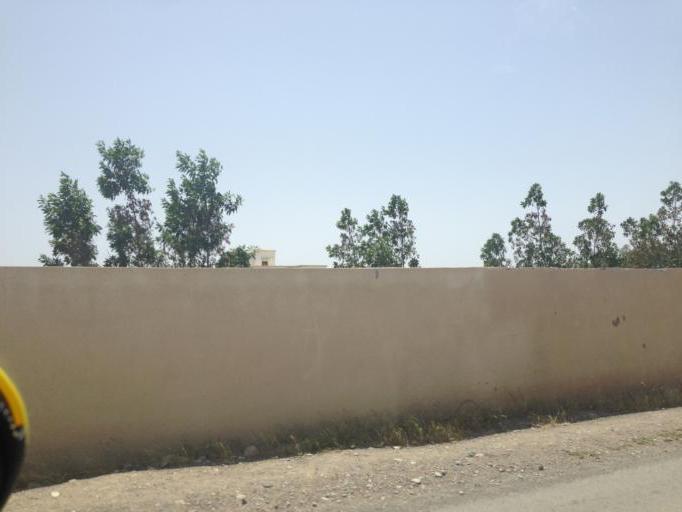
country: OM
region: Muhafazat Masqat
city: As Sib al Jadidah
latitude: 23.6855
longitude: 58.1168
